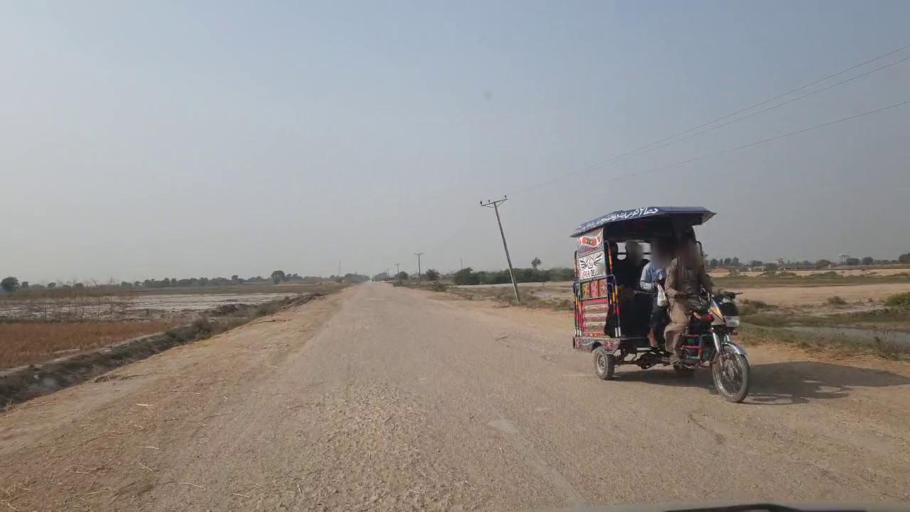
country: PK
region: Sindh
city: Matli
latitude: 25.0280
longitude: 68.6697
